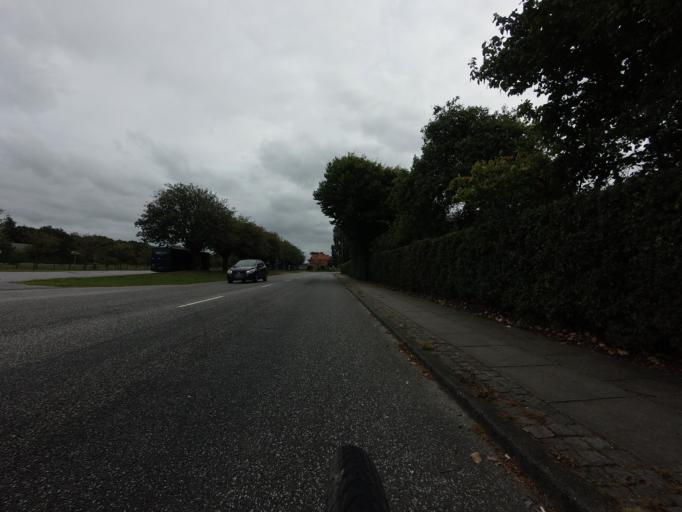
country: DK
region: South Denmark
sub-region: Billund Kommune
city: Grindsted
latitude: 55.7604
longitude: 8.9302
